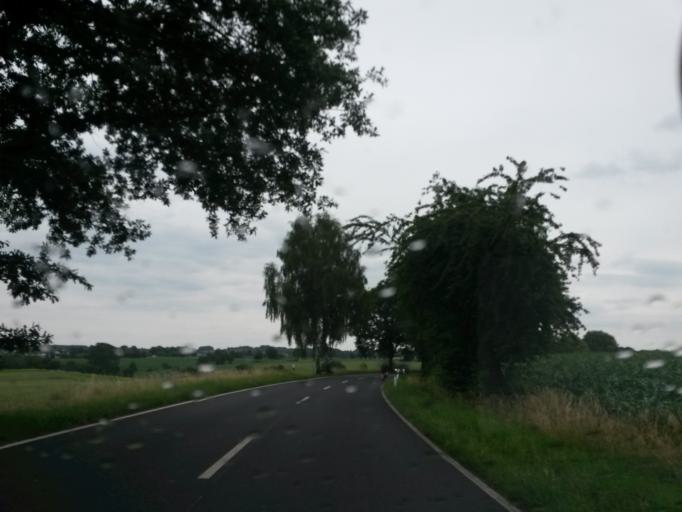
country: DE
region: North Rhine-Westphalia
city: Lohmar
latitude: 50.8534
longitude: 7.2569
